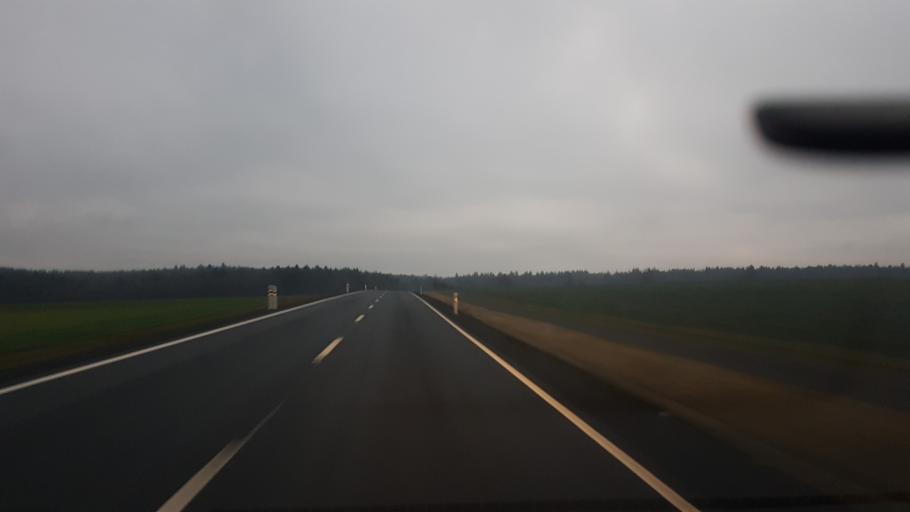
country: DE
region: Bavaria
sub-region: Regierungsbezirk Unterfranken
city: Ermershausen
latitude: 50.2164
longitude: 10.6128
